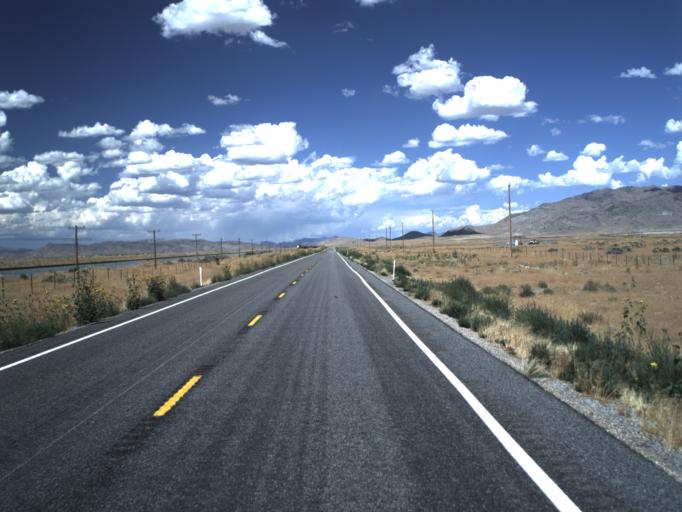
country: US
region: Utah
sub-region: Millard County
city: Delta
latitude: 39.5654
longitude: -112.3467
